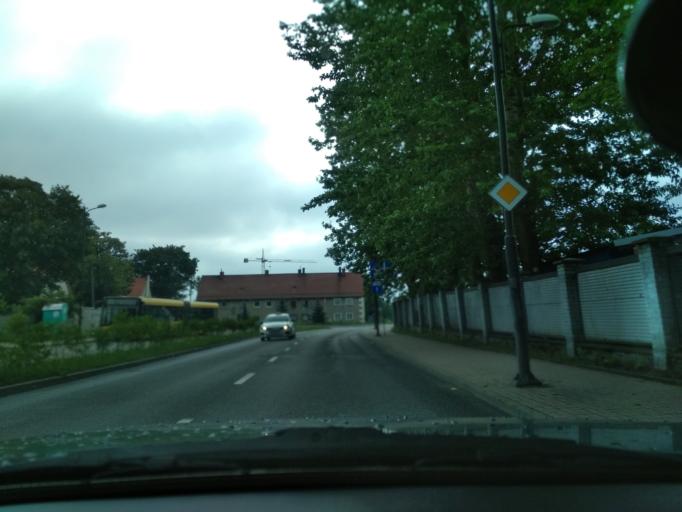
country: PL
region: Silesian Voivodeship
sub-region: Gliwice
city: Gliwice
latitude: 50.2749
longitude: 18.6727
